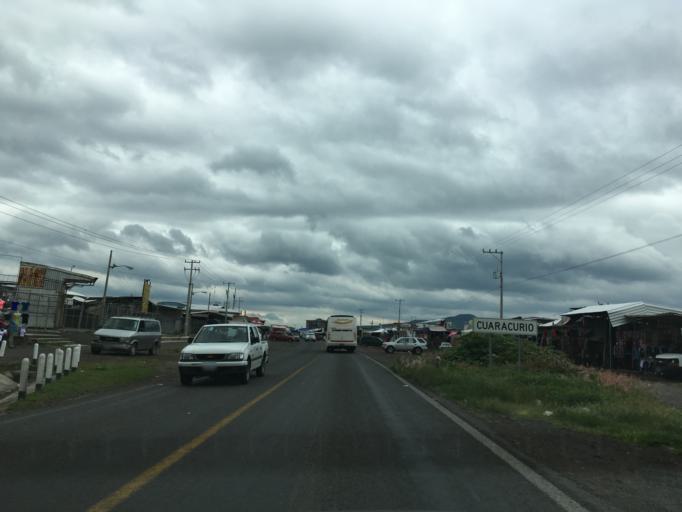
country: MX
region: Michoacan
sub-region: Cuitzeo
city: Cuamio
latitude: 20.0563
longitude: -101.1501
